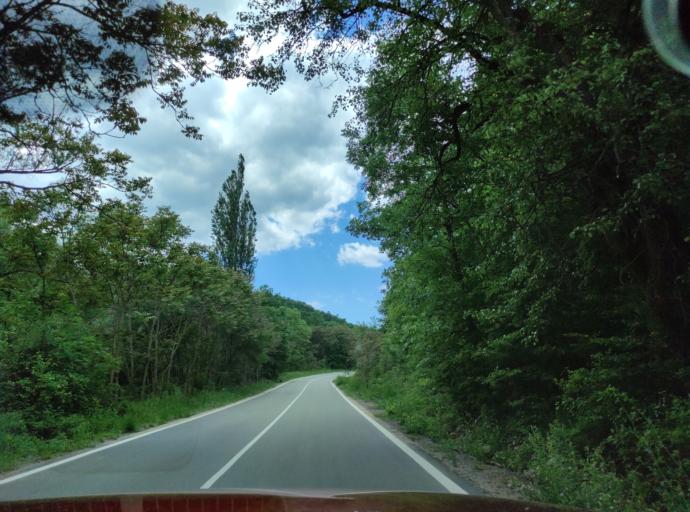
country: BG
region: Montana
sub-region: Obshtina Chiprovtsi
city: Chiprovtsi
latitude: 43.4576
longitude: 22.8960
